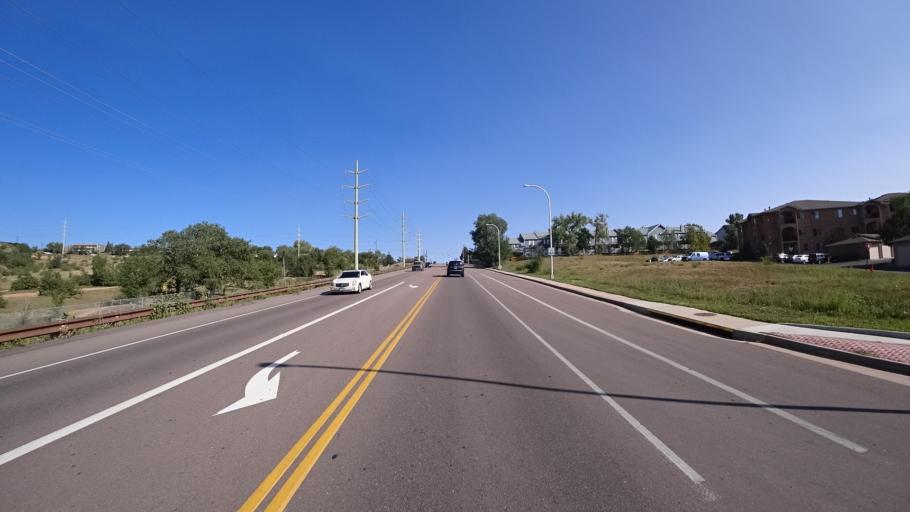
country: US
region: Colorado
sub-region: El Paso County
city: Colorado Springs
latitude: 38.8260
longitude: -104.8592
